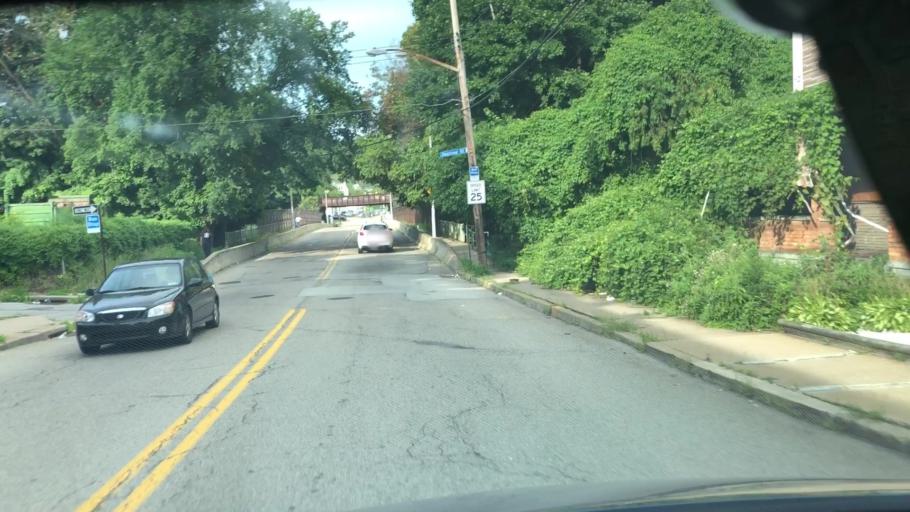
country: US
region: Pennsylvania
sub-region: Allegheny County
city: Aspinwall
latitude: 40.4620
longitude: -79.9066
